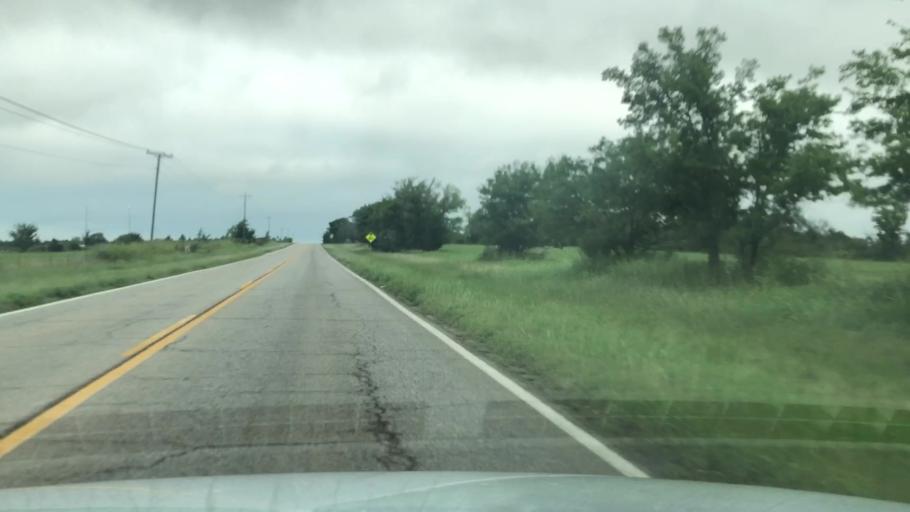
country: US
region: Oklahoma
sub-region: Nowata County
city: Nowata
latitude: 36.7075
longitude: -95.6550
